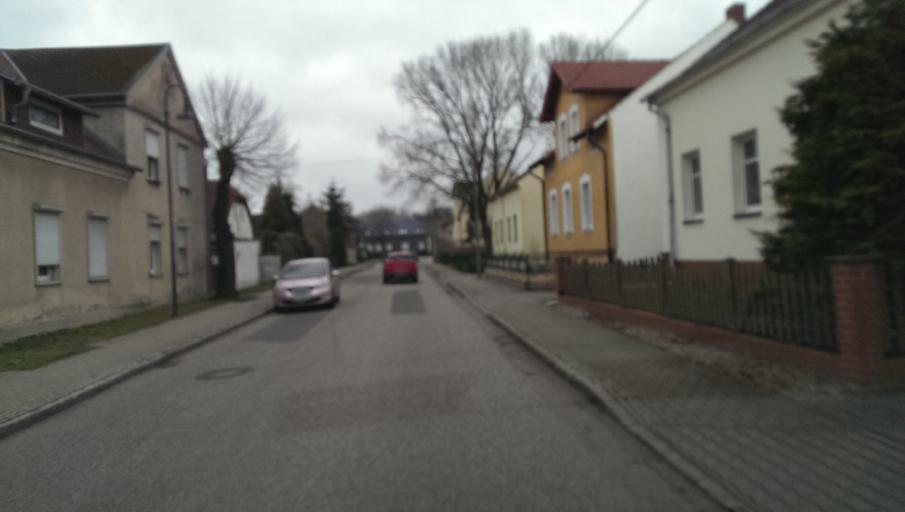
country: DE
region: Brandenburg
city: Ludwigsfelde
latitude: 52.2963
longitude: 13.3162
